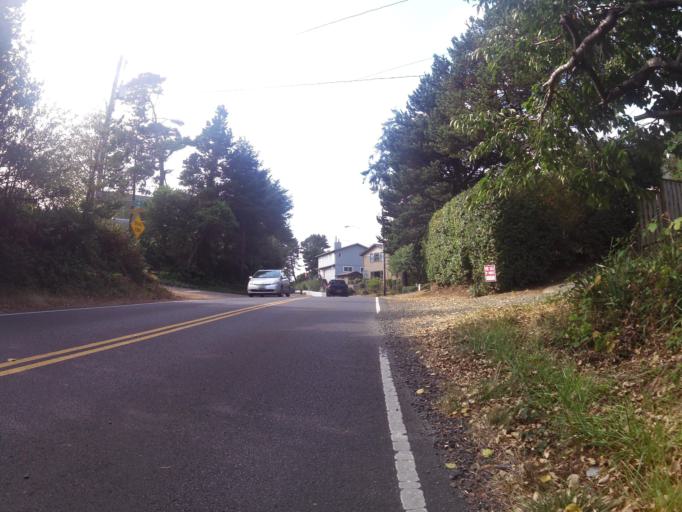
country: US
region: Oregon
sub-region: Lincoln County
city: Newport
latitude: 44.6500
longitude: -124.0566
